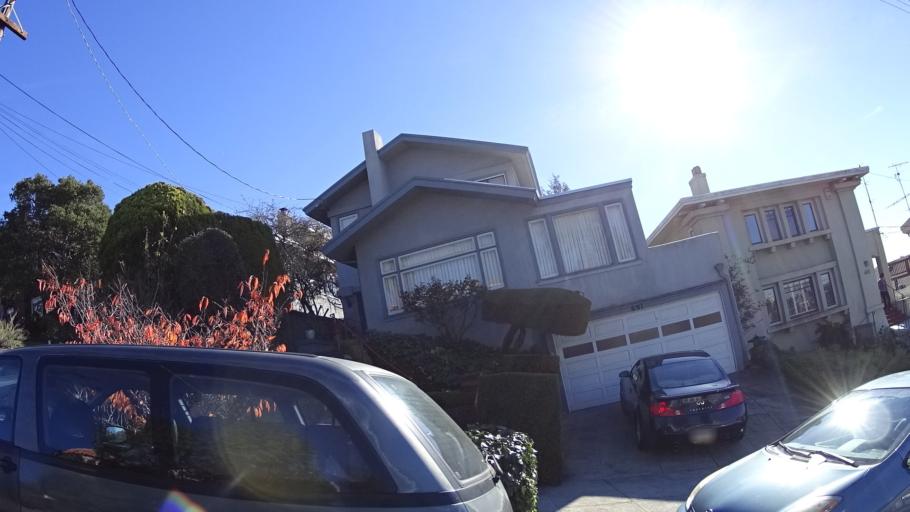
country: US
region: California
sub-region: Alameda County
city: Piedmont
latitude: 37.8124
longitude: -122.2384
